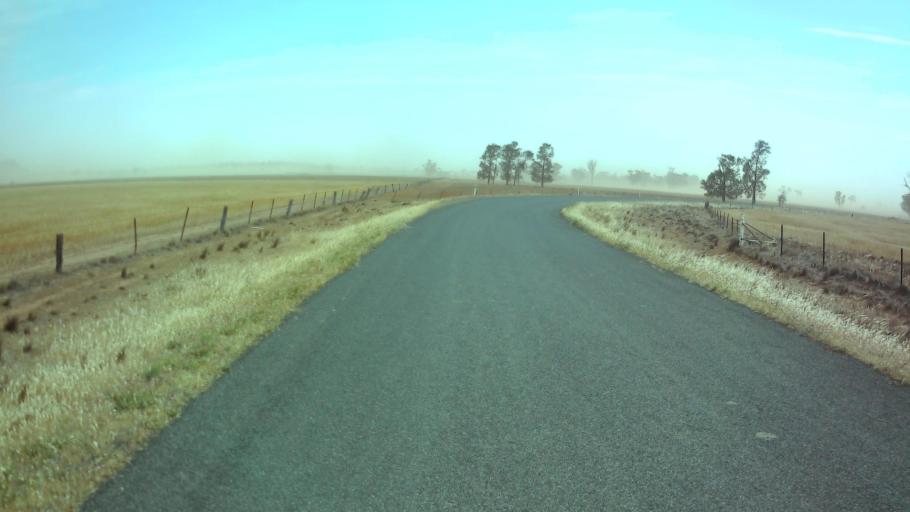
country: AU
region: New South Wales
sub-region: Weddin
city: Grenfell
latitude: -33.7385
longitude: 147.9931
